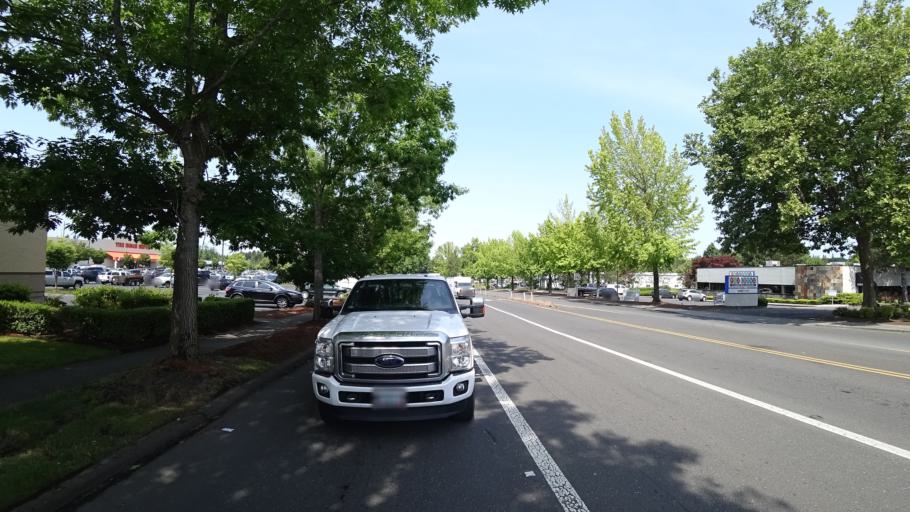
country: US
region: Oregon
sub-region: Washington County
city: Cedar Mill
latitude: 45.5249
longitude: -122.8154
